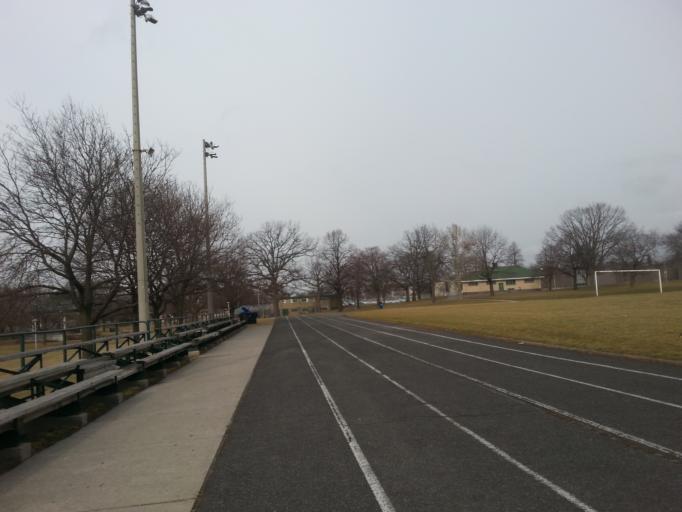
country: CA
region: Ontario
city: Toronto
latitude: 43.6728
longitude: -79.4511
